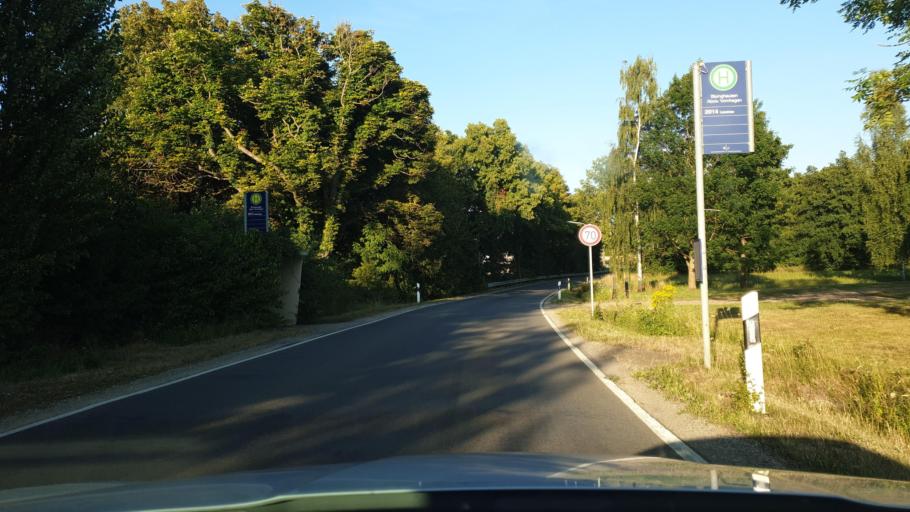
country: DE
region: Lower Saxony
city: Heuerssen
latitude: 52.3167
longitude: 9.2519
